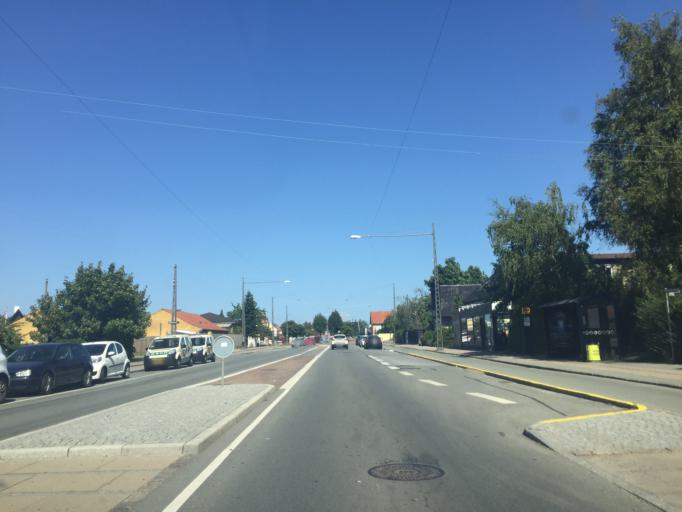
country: DK
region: Capital Region
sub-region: Tarnby Kommune
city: Tarnby
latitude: 55.6398
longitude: 12.5890
